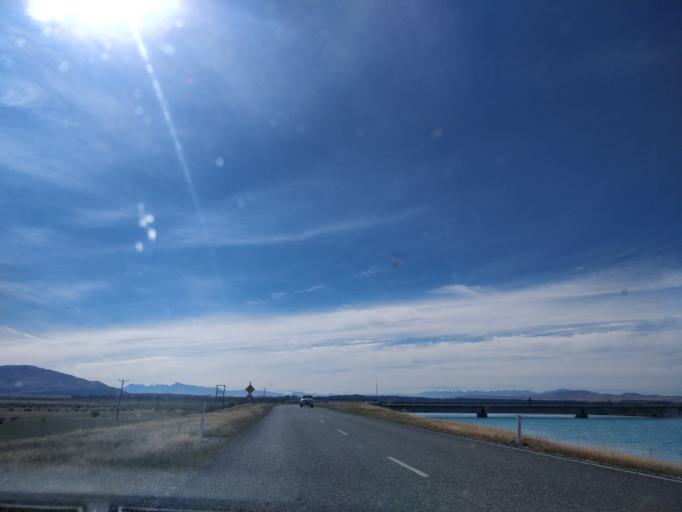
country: NZ
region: Otago
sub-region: Queenstown-Lakes District
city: Wanaka
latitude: -44.2208
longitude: 170.0492
